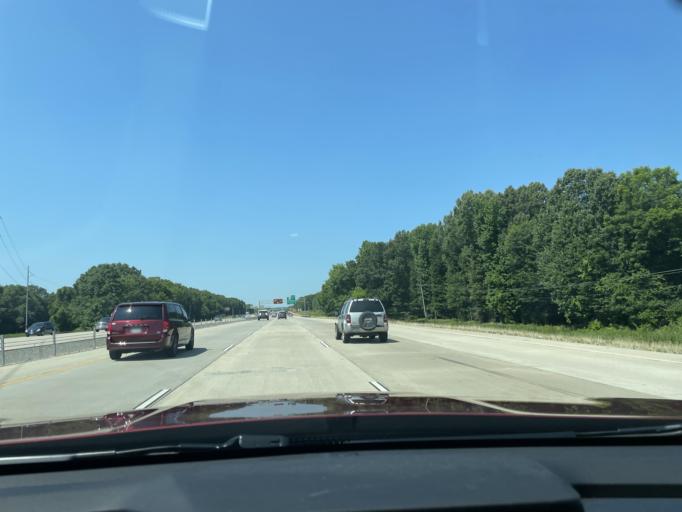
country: US
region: Arkansas
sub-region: Pulaski County
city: Jacksonville
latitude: 34.8564
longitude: -92.1347
